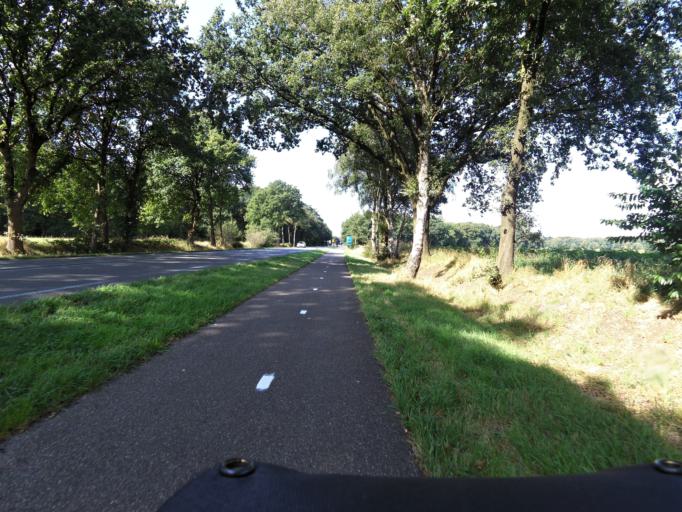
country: NL
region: Gelderland
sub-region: Gemeente Apeldoorn
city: Uddel
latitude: 52.2432
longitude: 5.7582
